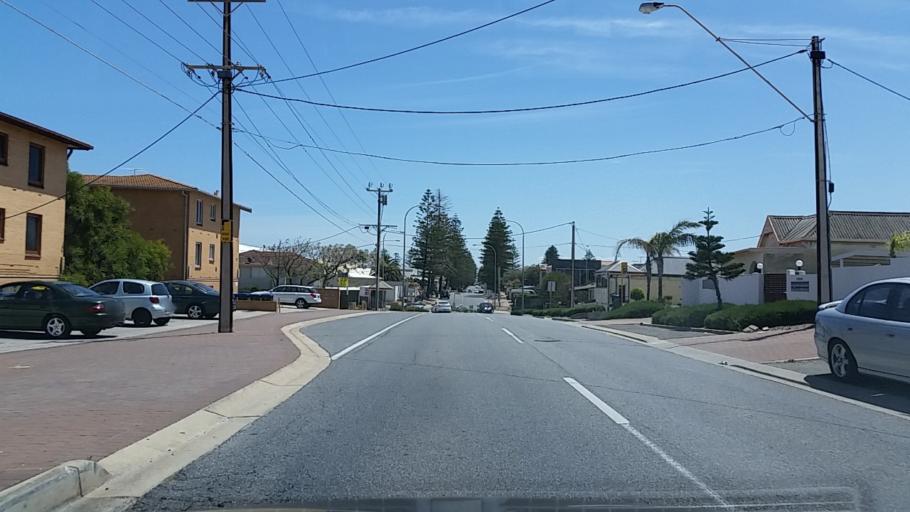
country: AU
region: South Australia
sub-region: Charles Sturt
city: Grange
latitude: -34.9085
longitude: 138.4913
